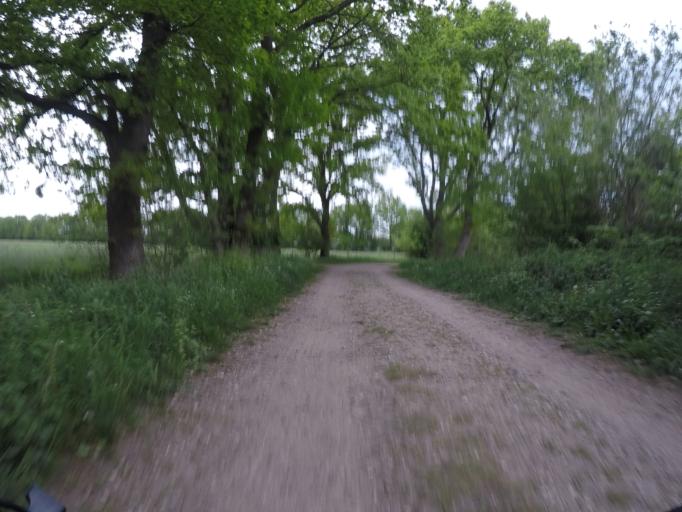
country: DE
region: Schleswig-Holstein
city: Henstedt-Ulzburg
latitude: 53.7663
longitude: 10.0145
